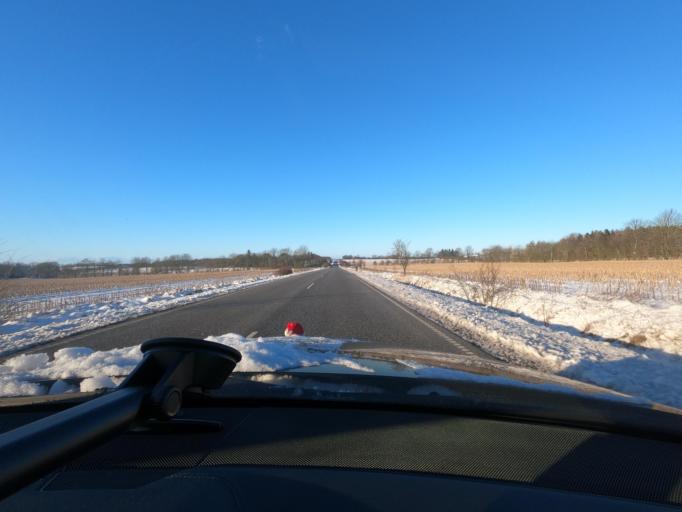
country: DK
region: South Denmark
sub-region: Tonder Kommune
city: Toftlund
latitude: 55.1152
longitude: 9.1655
